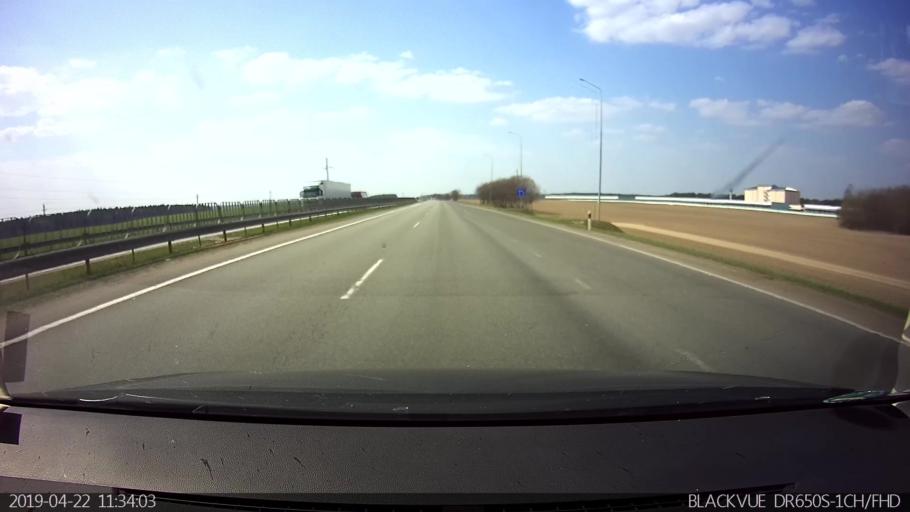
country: BY
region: Minsk
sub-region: Smalyavitski Rayon
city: Oktjabr'skij
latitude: 54.0175
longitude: 28.2040
